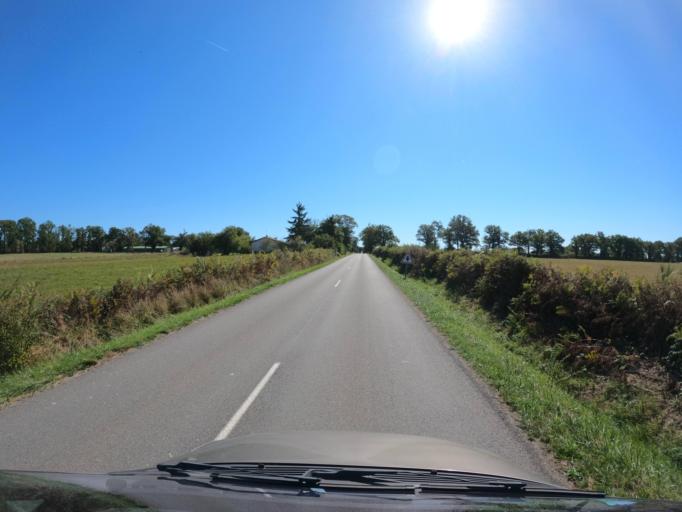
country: FR
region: Limousin
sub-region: Departement de la Haute-Vienne
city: Le Dorat
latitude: 46.2711
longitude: 1.0240
